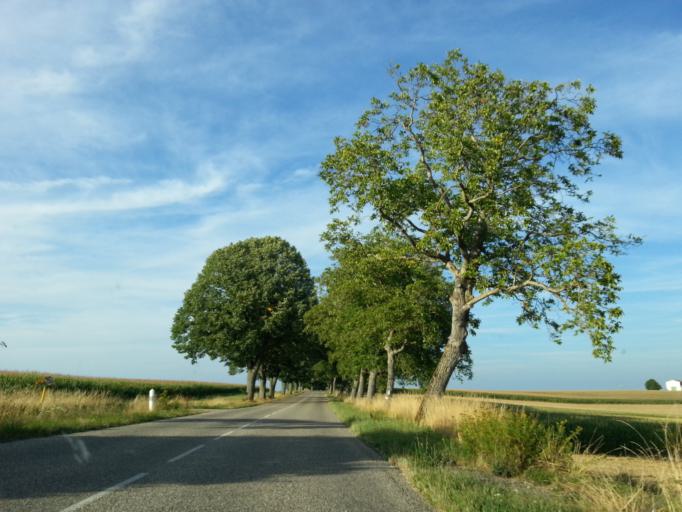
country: FR
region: Alsace
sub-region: Departement du Bas-Rhin
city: Soultz-sous-Forets
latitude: 48.9232
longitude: 7.8653
